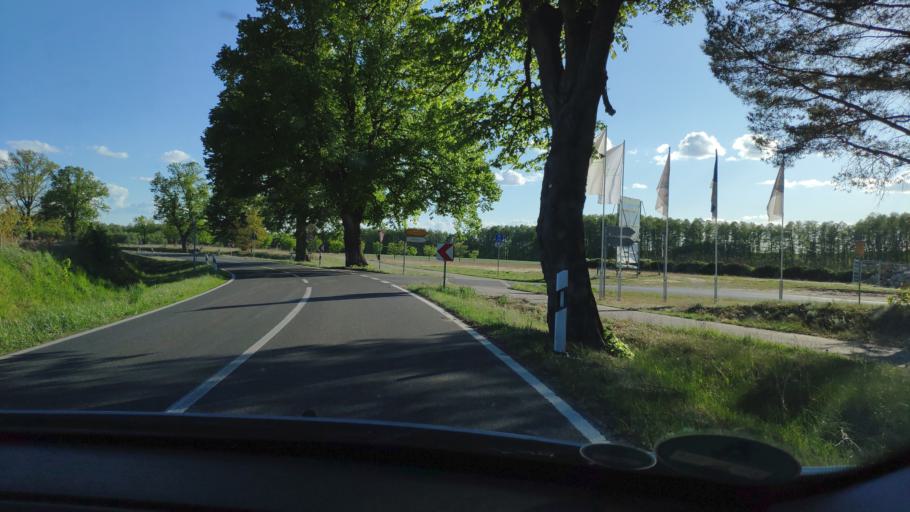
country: DE
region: Mecklenburg-Vorpommern
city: Rechlin
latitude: 53.2998
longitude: 12.8130
